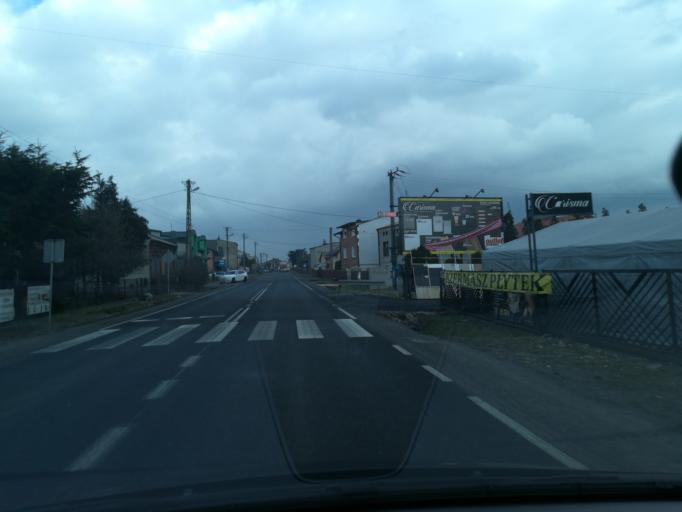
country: PL
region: Lodz Voivodeship
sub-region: Powiat radomszczanski
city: Radomsko
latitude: 51.0777
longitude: 19.3905
